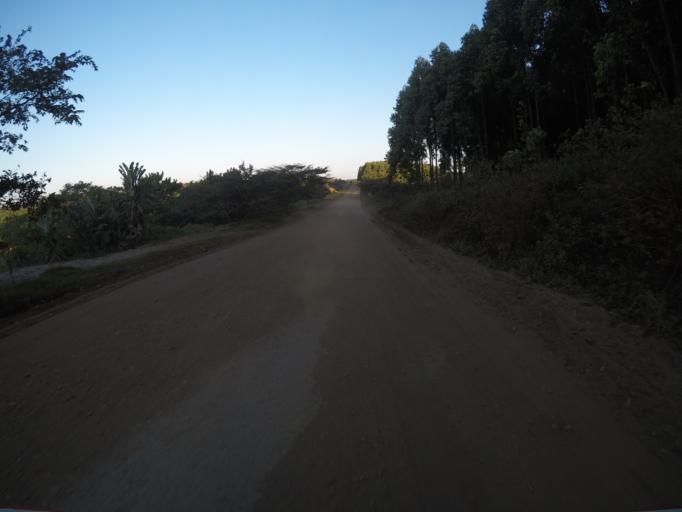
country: ZA
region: KwaZulu-Natal
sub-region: uThungulu District Municipality
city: KwaMbonambi
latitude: -28.6772
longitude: 32.1195
